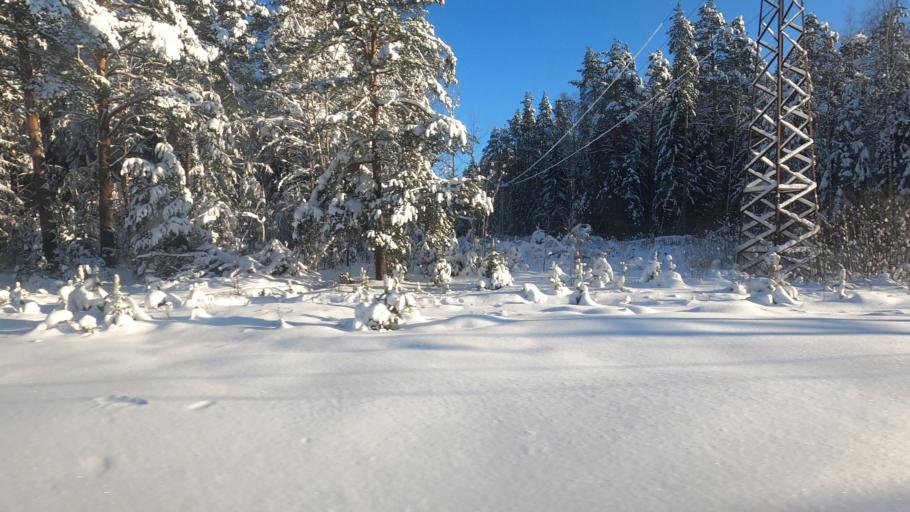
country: RU
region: Moskovskaya
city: Novo-Nikol'skoye
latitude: 56.5543
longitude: 37.5649
